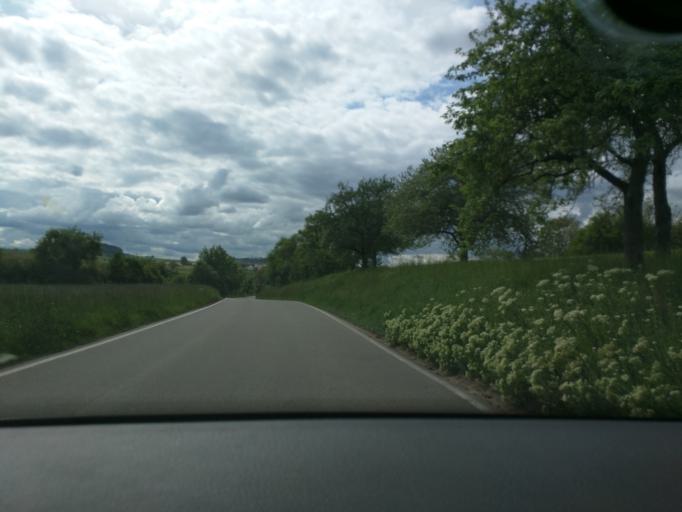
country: DE
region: Baden-Wuerttemberg
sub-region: Tuebingen Region
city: Rottenburg
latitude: 48.5025
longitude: 8.9524
